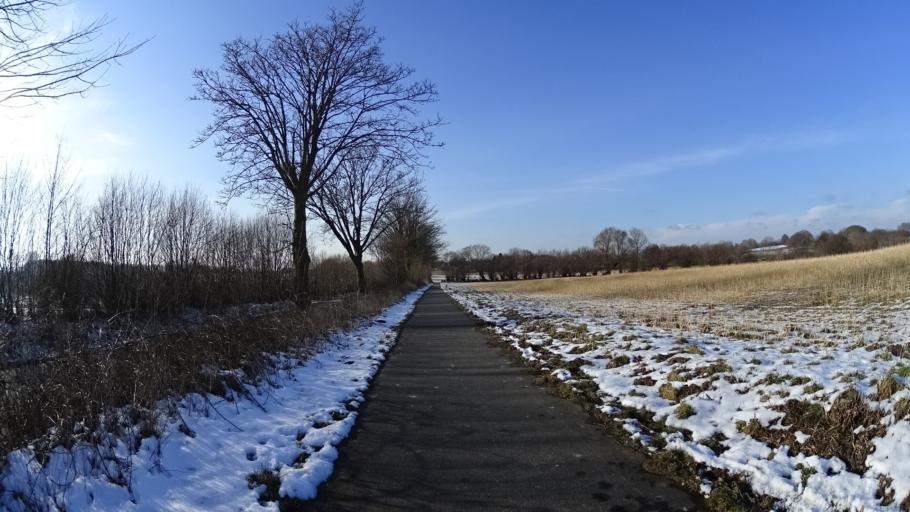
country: DE
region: Schleswig-Holstein
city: Martensrade
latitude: 54.2825
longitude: 10.3905
